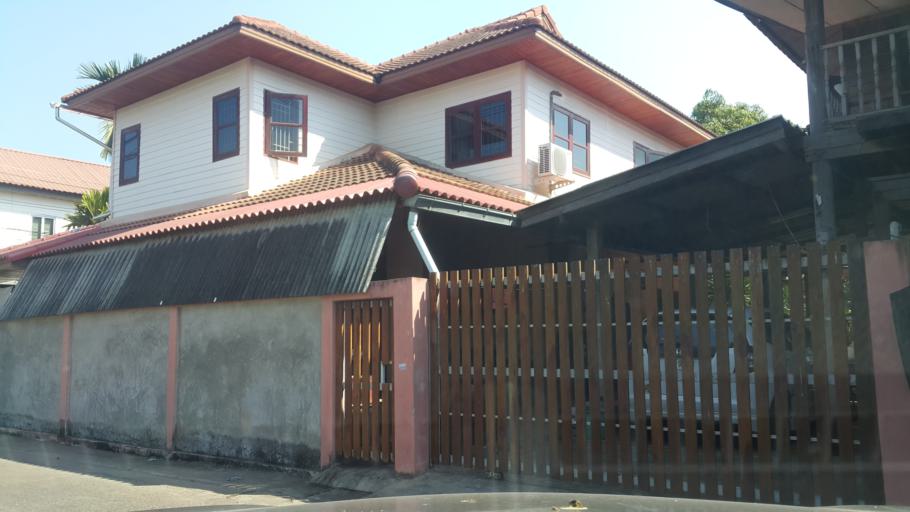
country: TH
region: Changwat Udon Thani
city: Udon Thani
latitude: 17.3913
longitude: 102.7933
